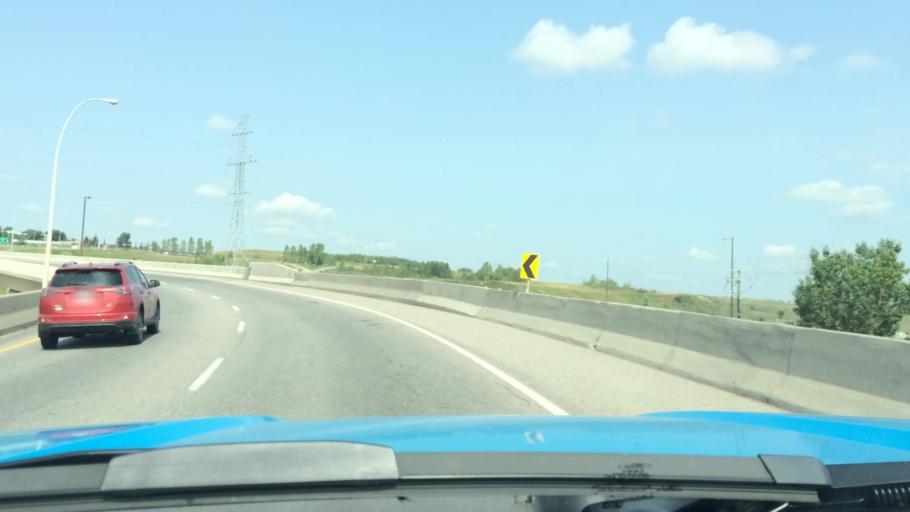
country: CA
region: Alberta
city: Calgary
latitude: 51.1256
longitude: -114.0446
